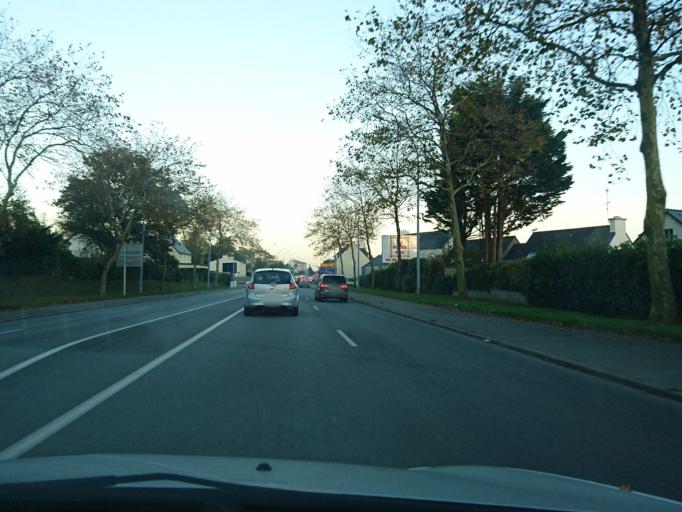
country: FR
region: Brittany
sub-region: Departement du Finistere
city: Brest
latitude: 48.4130
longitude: -4.4996
